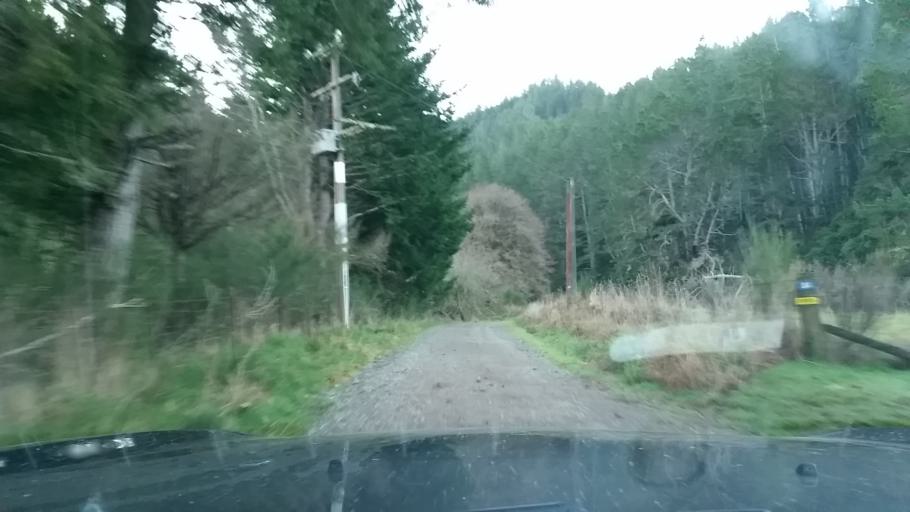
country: NZ
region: Marlborough
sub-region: Marlborough District
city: Blenheim
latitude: -41.4693
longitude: 173.7439
